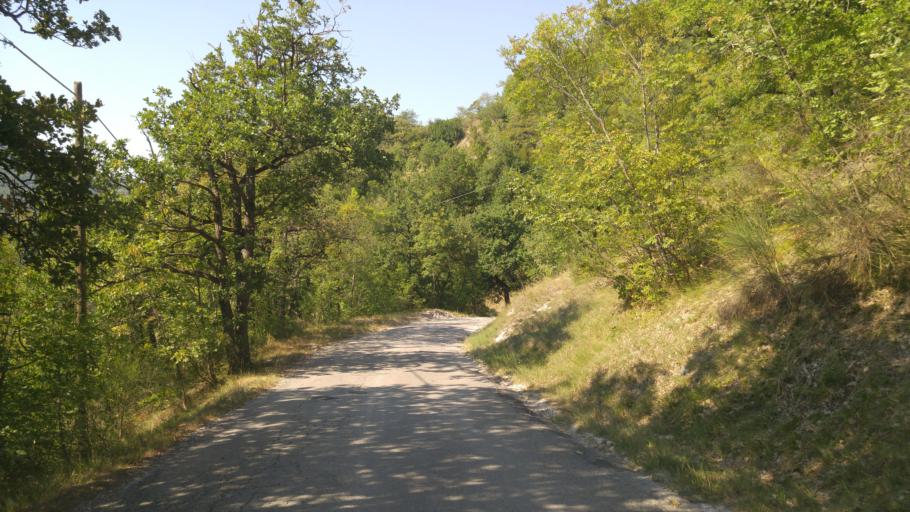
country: IT
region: The Marches
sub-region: Provincia di Pesaro e Urbino
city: Fossombrone
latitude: 43.6787
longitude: 12.8048
